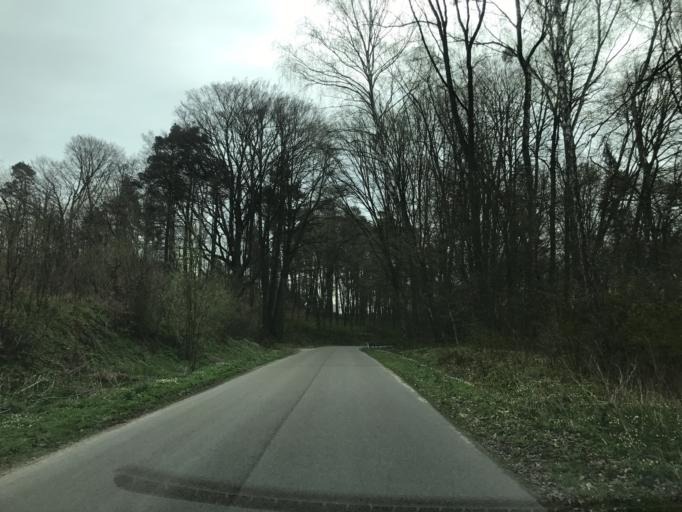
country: PL
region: Warmian-Masurian Voivodeship
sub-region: Powiat ostrodzki
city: Gierzwald
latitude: 53.6375
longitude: 20.0785
